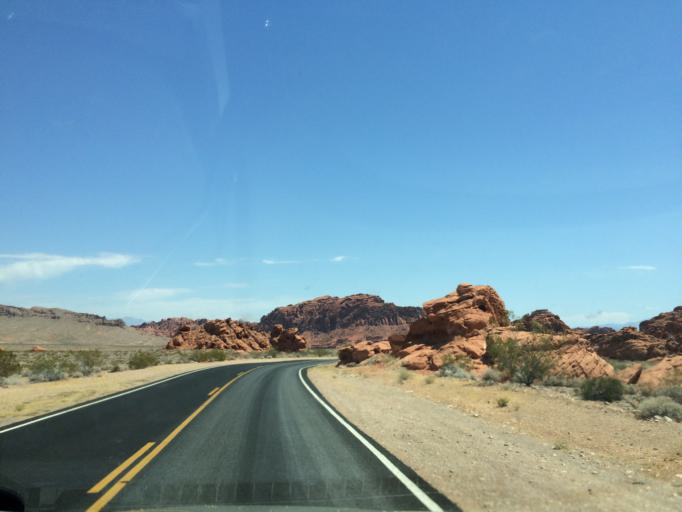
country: US
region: Nevada
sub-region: Clark County
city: Moapa Valley
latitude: 36.4140
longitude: -114.5480
